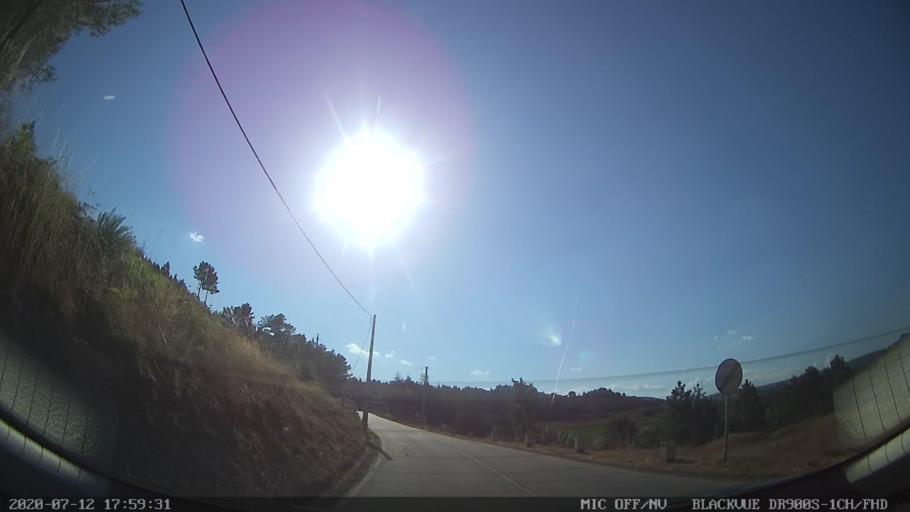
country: PT
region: Viseu
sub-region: Sao Joao da Pesqueira
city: Sao Joao da Pesqueira
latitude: 41.2622
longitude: -7.4451
